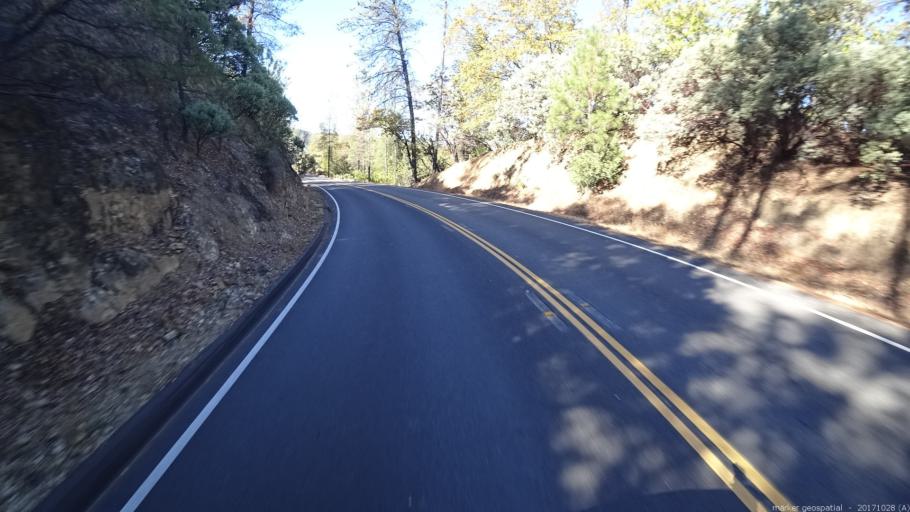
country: US
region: California
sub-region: Shasta County
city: Shasta
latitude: 40.6153
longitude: -122.5659
